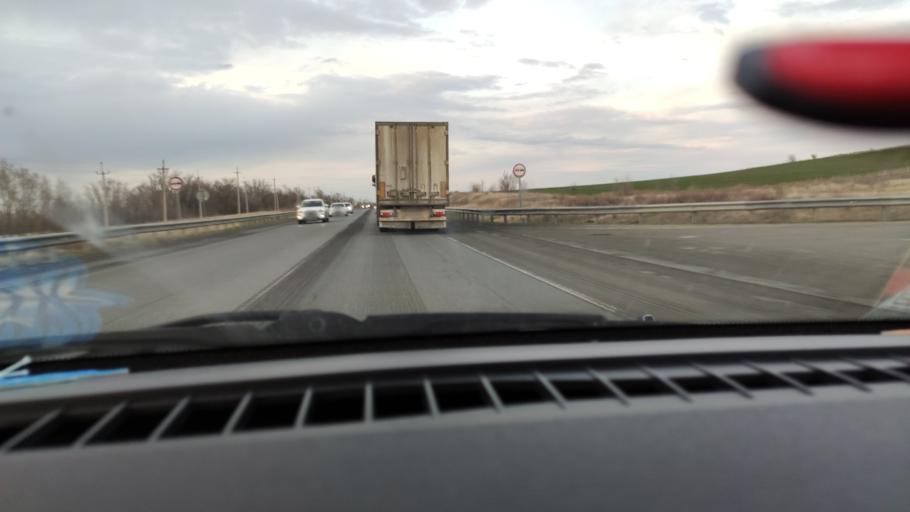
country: RU
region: Saratov
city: Shumeyka
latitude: 51.7860
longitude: 46.1373
